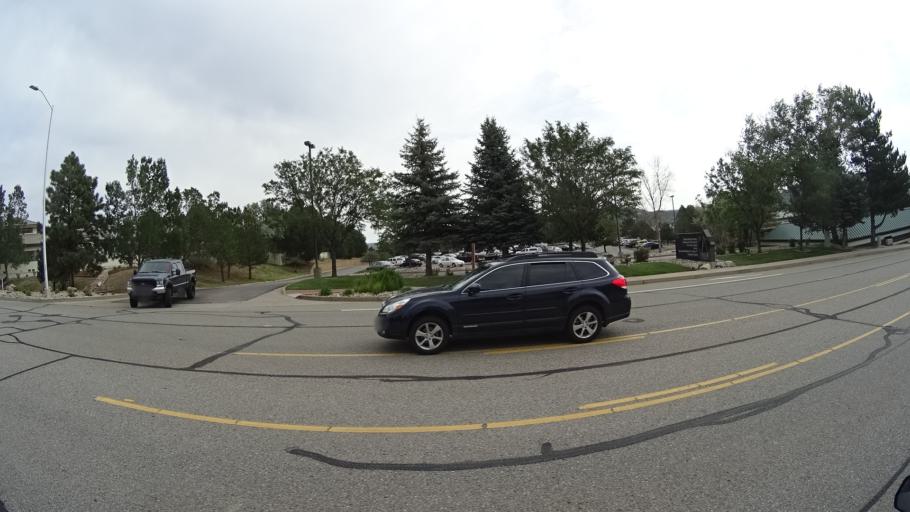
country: US
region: Colorado
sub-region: El Paso County
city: Colorado Springs
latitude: 38.9183
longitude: -104.8250
